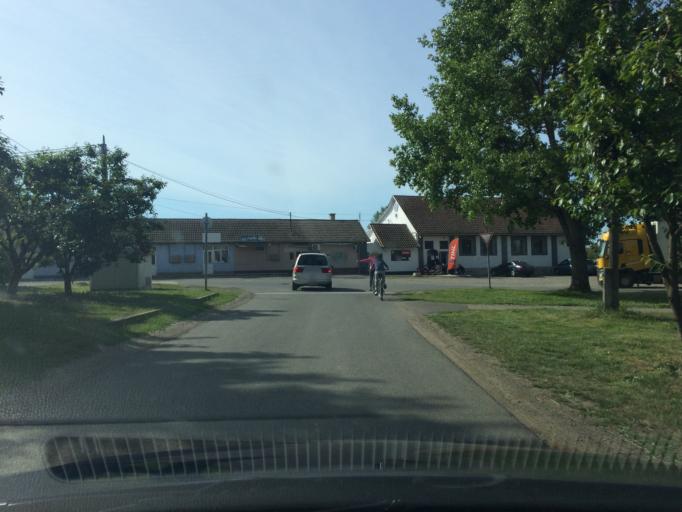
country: HU
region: Szabolcs-Szatmar-Bereg
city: Tiszavasvari
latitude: 47.9590
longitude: 21.3533
